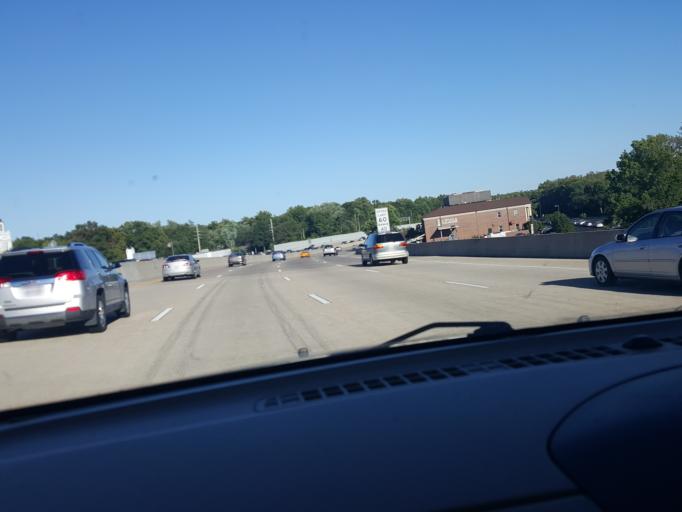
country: US
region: Missouri
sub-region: Saint Louis County
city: Ladue
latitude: 38.6362
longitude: -90.3943
